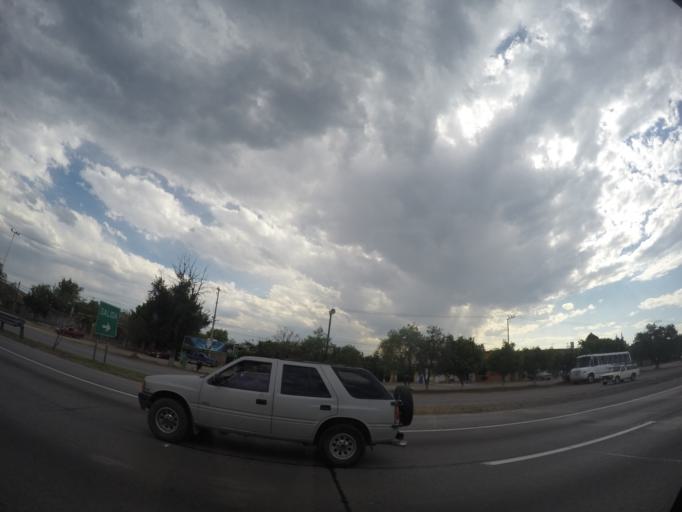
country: MX
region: Queretaro
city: San Juan del Rio
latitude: 20.4031
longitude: -100.0298
